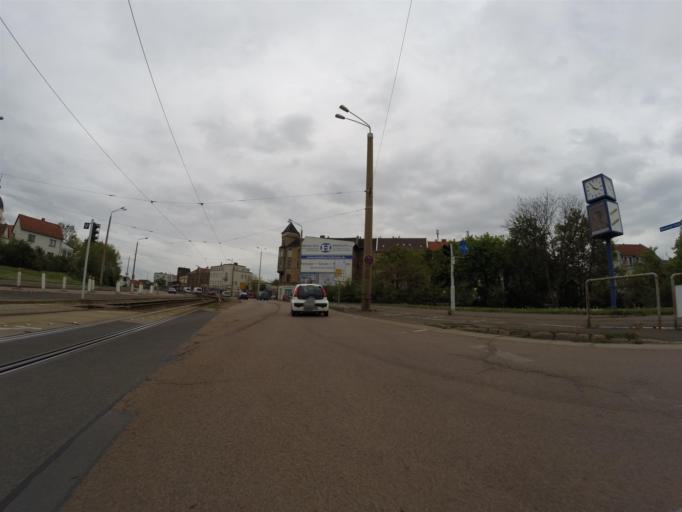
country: DE
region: Saxony-Anhalt
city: Schkopau
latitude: 51.4250
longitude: 11.9854
